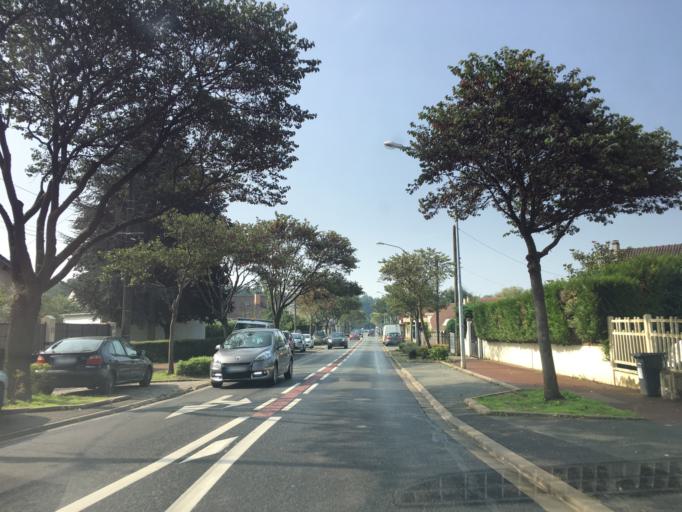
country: FR
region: Ile-de-France
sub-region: Departement du Val-de-Marne
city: Sucy-en-Brie
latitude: 48.7697
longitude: 2.5431
